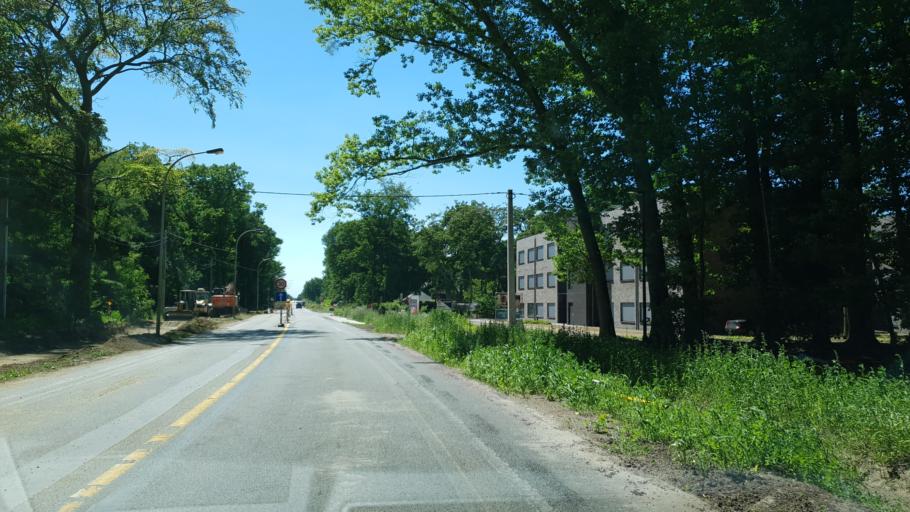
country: BE
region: Flanders
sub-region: Provincie Antwerpen
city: Vorselaar
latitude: 51.1767
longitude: 4.7680
